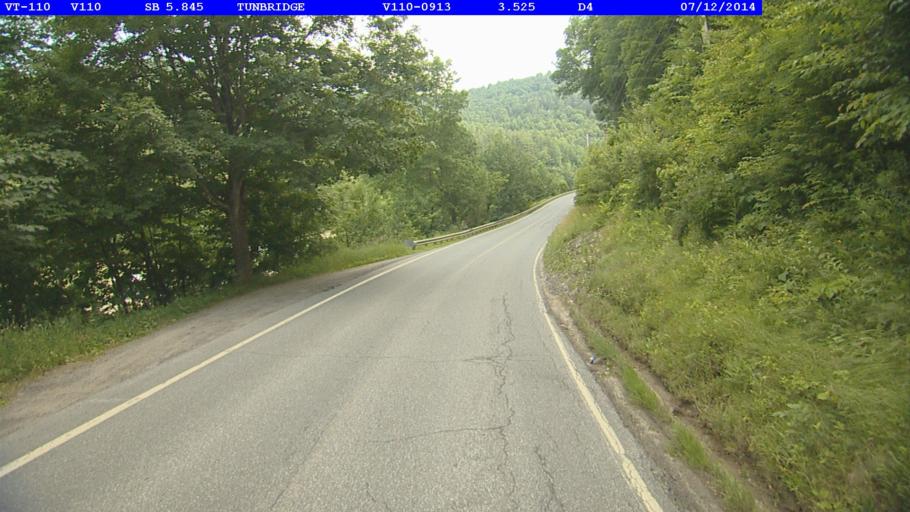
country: US
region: Vermont
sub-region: Orange County
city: Chelsea
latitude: 43.8961
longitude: -72.4852
